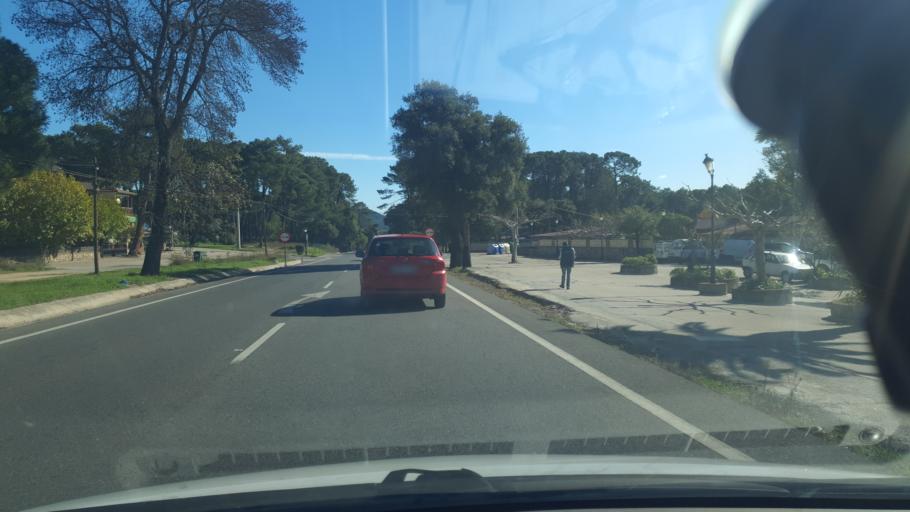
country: ES
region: Castille and Leon
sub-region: Provincia de Avila
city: La Adrada
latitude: 40.3104
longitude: -4.6569
